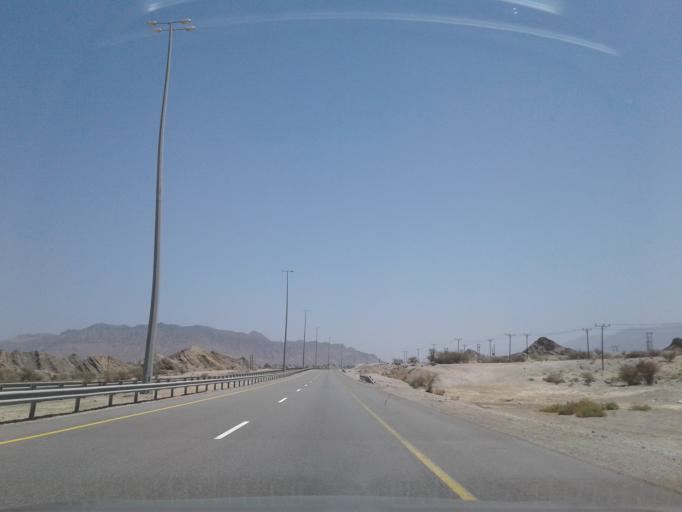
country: OM
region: Muhafazat Masqat
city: Muscat
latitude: 23.3472
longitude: 58.6926
